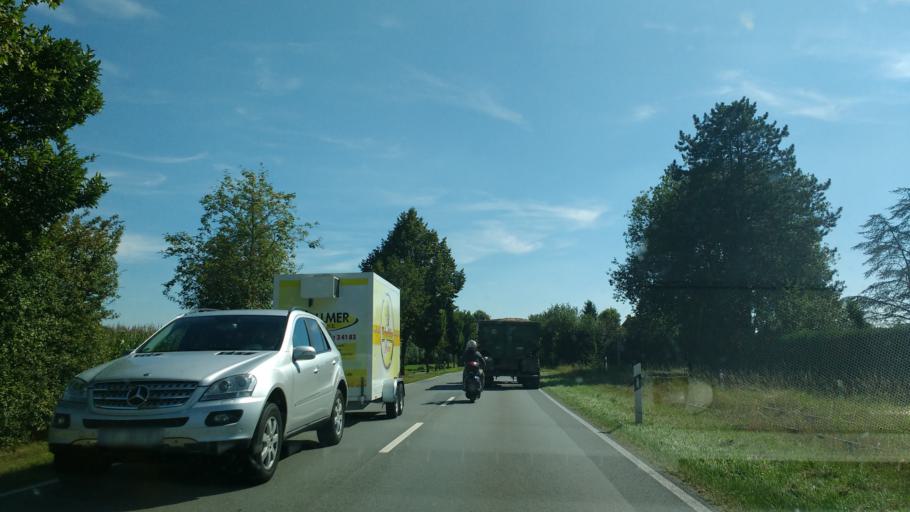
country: DE
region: North Rhine-Westphalia
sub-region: Regierungsbezirk Detmold
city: Rheda-Wiedenbruck
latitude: 51.8214
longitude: 8.3133
